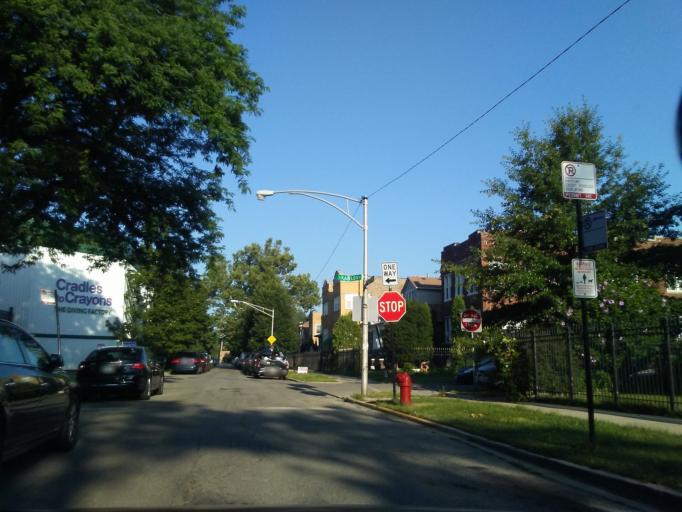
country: US
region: Illinois
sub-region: Cook County
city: Lincolnwood
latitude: 41.9336
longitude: -87.7292
